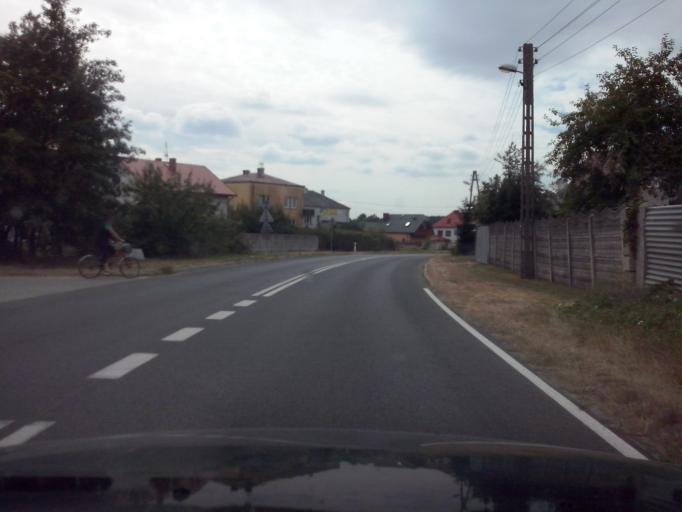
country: PL
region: Swietokrzyskie
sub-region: Powiat kielecki
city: Rakow
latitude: 50.6751
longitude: 21.0479
